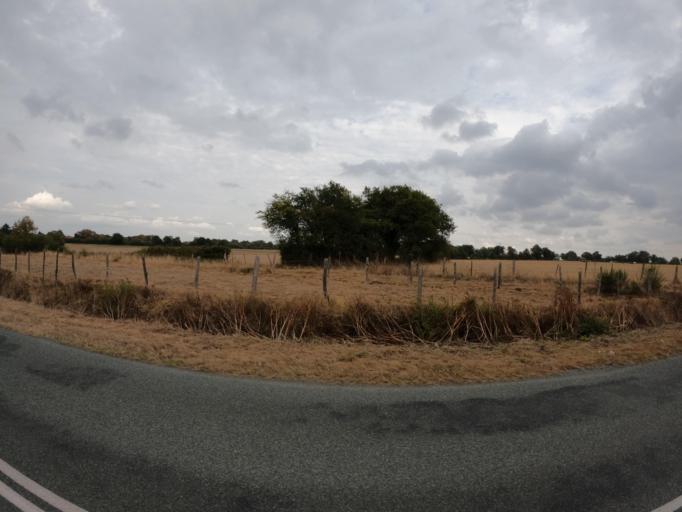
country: FR
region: Pays de la Loire
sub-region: Departement de Maine-et-Loire
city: Le Longeron
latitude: 47.0259
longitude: -1.0502
